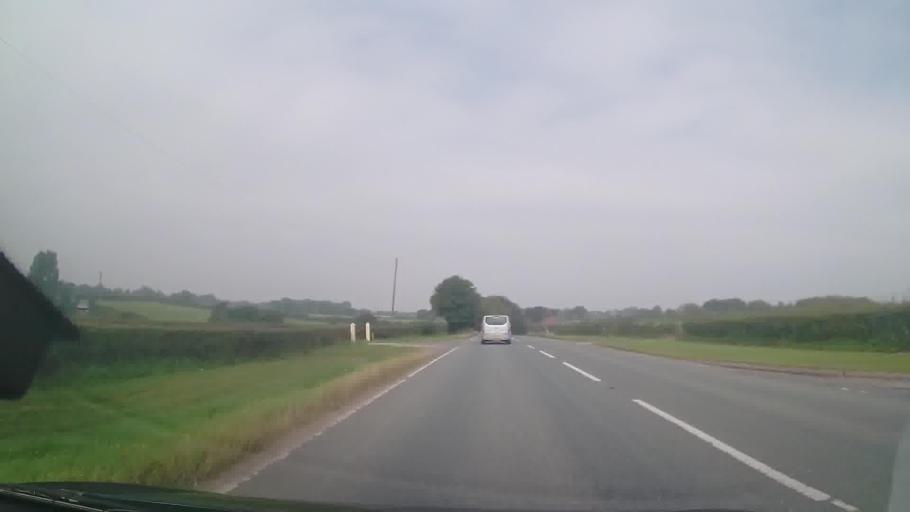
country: GB
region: England
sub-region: Warrington
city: Stretton
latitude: 53.3114
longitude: -2.5836
